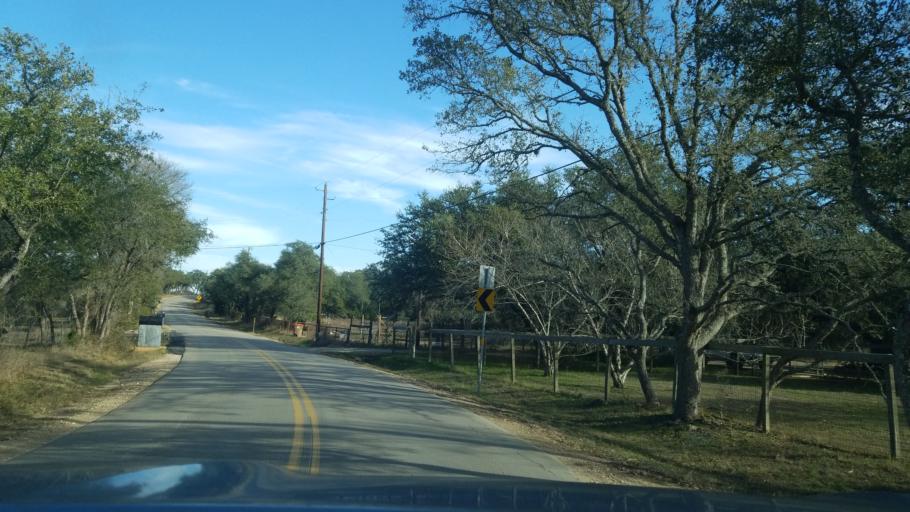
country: US
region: Texas
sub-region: Comal County
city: Canyon Lake
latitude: 29.7801
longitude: -98.2791
